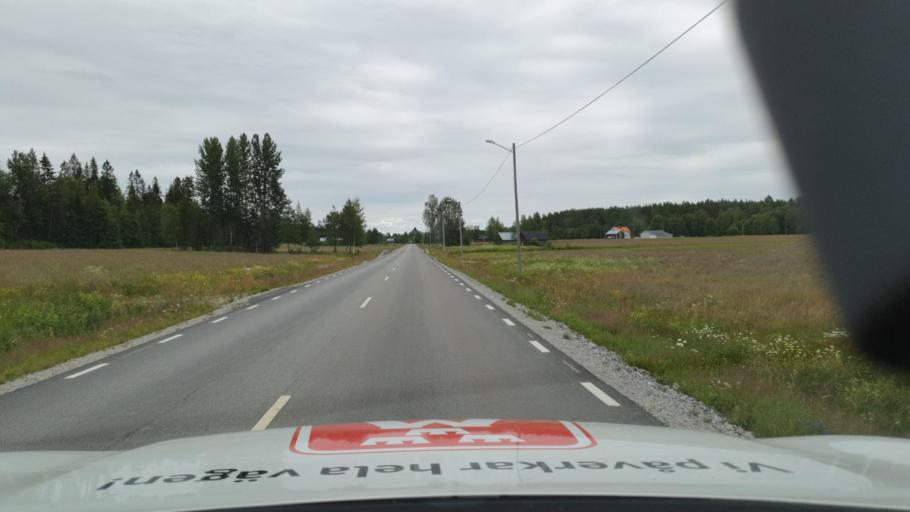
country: SE
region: Vaesterbotten
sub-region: Nordmalings Kommun
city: Nordmaling
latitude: 63.5400
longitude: 19.3688
